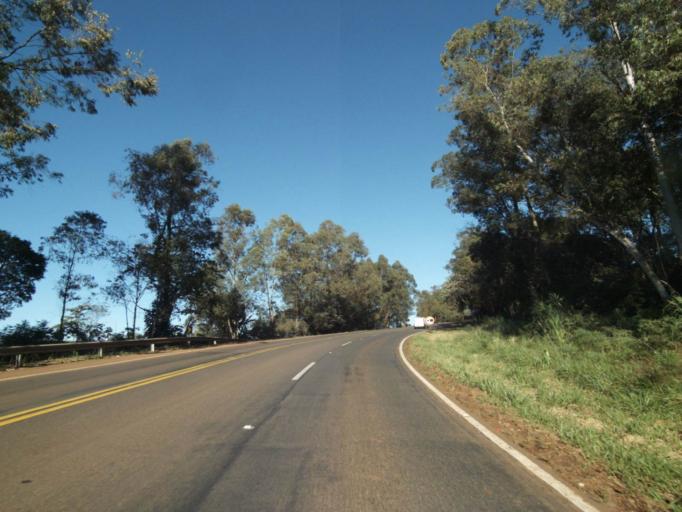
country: BR
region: Parana
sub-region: Faxinal
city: Faxinal
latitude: -23.7488
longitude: -51.1304
